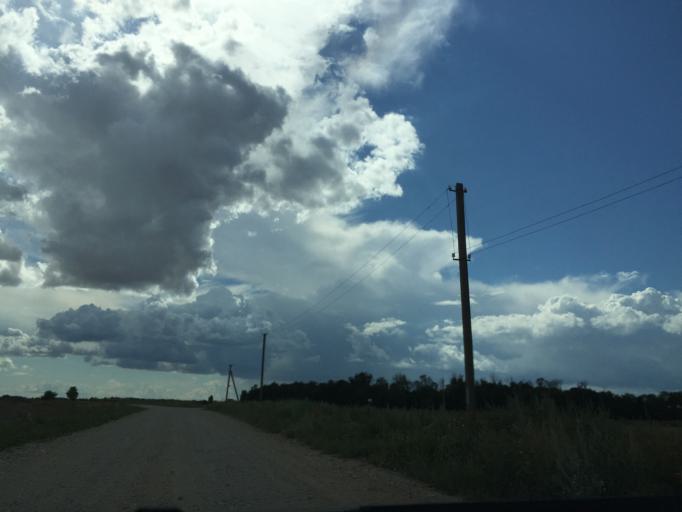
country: LT
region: Siauliu apskritis
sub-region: Joniskis
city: Joniskis
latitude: 56.3370
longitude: 23.6015
